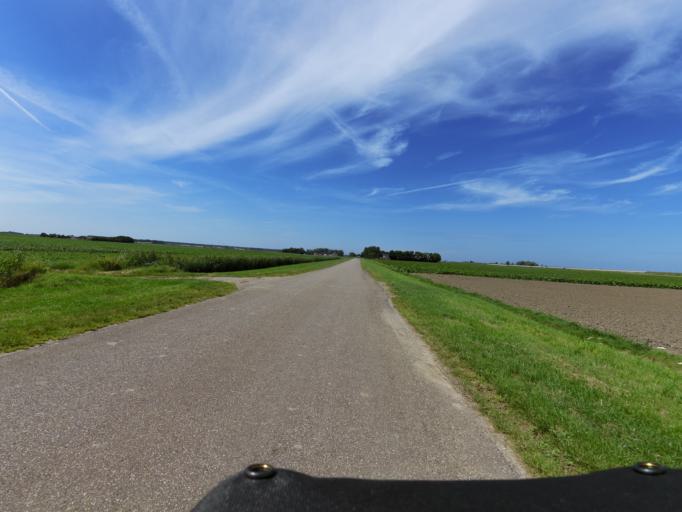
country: NL
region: South Holland
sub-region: Gemeente Goeree-Overflakkee
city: Dirksland
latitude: 51.7964
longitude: 4.1006
